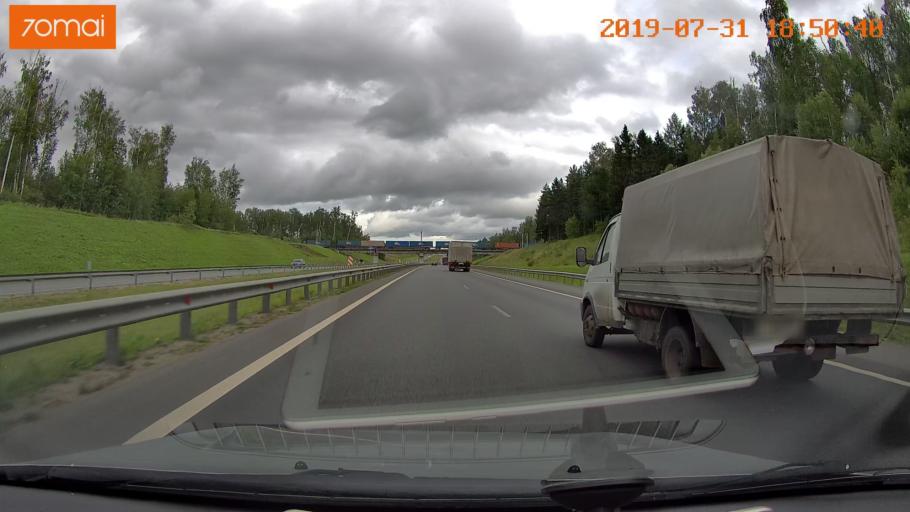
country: RU
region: Moskovskaya
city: Troitskoye
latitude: 55.2274
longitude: 38.5876
